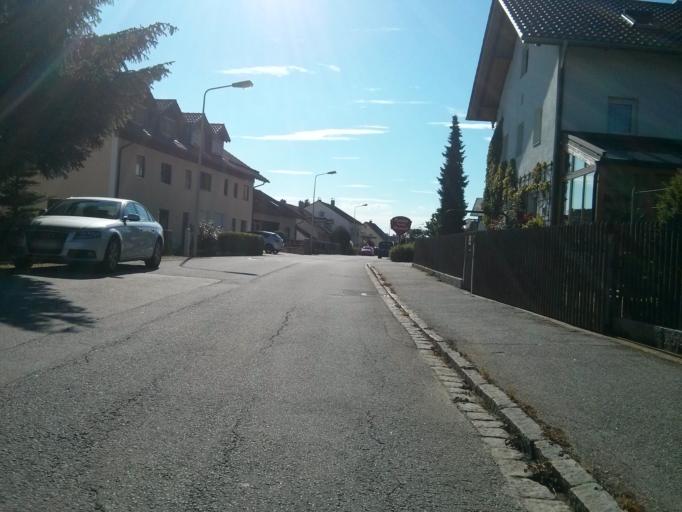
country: DE
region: Bavaria
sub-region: Lower Bavaria
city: Metten
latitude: 48.8230
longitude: 12.9144
